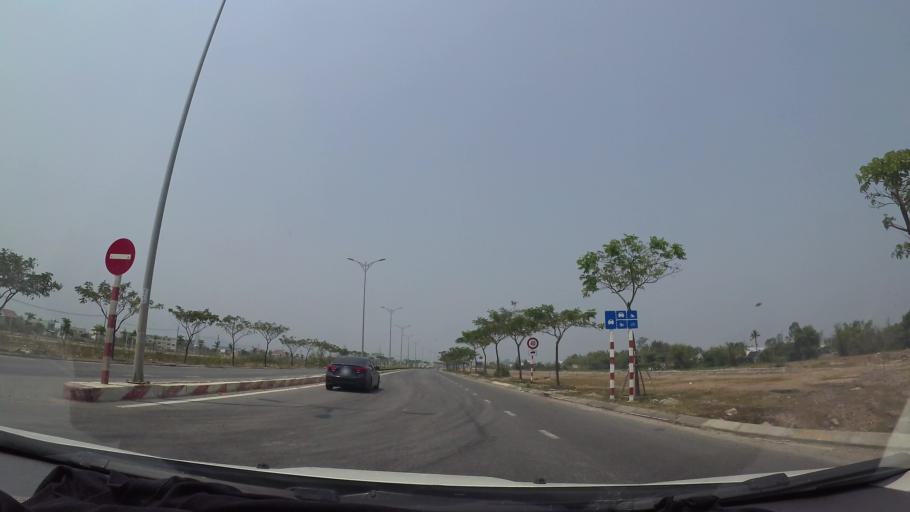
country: VN
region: Da Nang
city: Ngu Hanh Son
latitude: 15.9910
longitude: 108.2376
